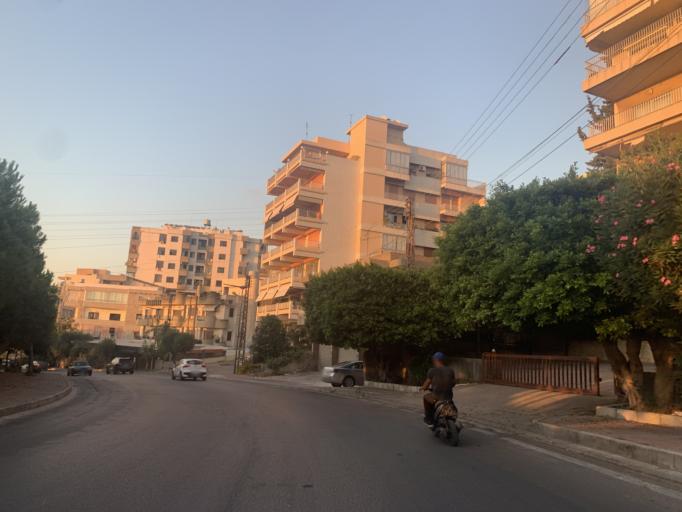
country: LB
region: Mont-Liban
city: Djounie
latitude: 33.9625
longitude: 35.6239
